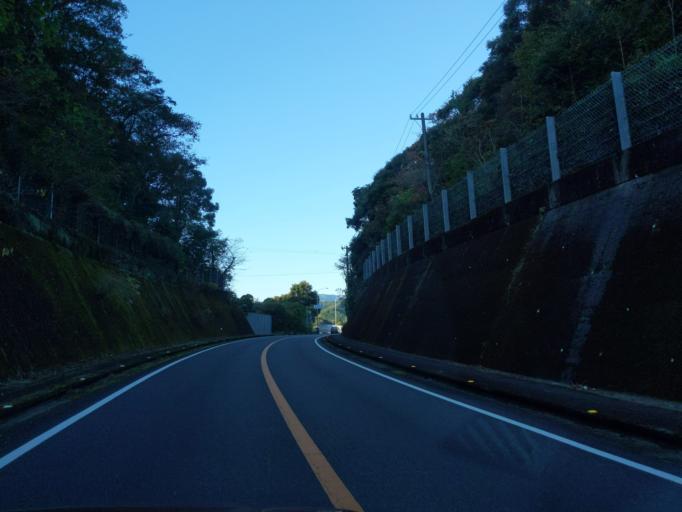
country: JP
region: Kochi
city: Muroto-misakicho
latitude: 33.5469
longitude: 134.3037
